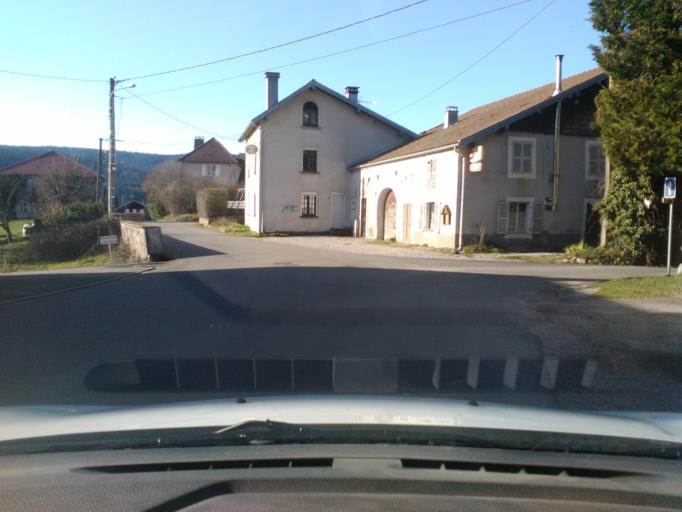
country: FR
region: Lorraine
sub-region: Departement des Vosges
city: Vecoux
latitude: 47.9798
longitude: 6.6390
